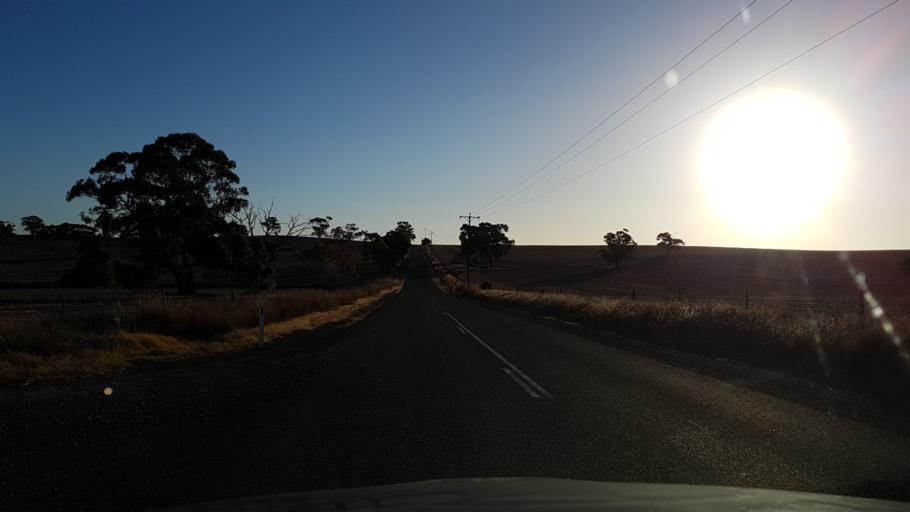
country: AU
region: South Australia
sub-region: Clare and Gilbert Valleys
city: Clare
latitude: -34.0179
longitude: 138.7157
